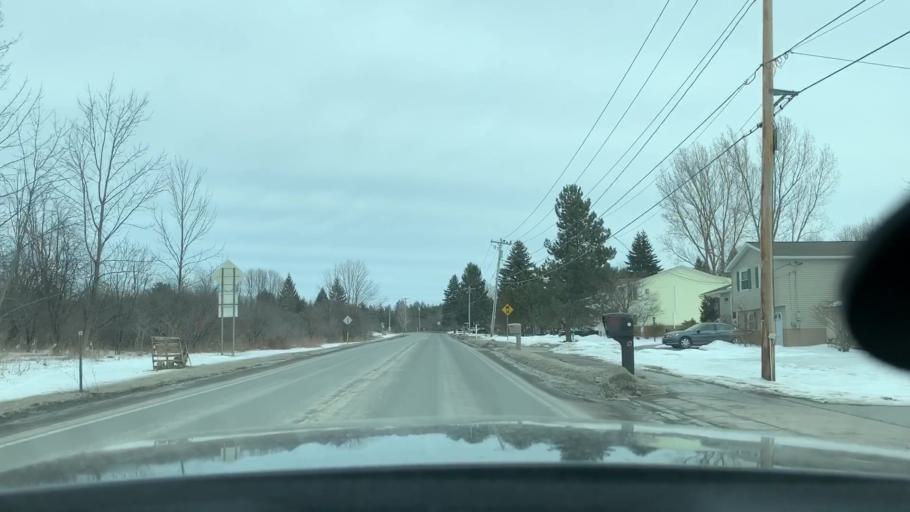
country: US
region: New York
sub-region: Oneida County
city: Washington Mills
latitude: 43.0563
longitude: -75.2518
